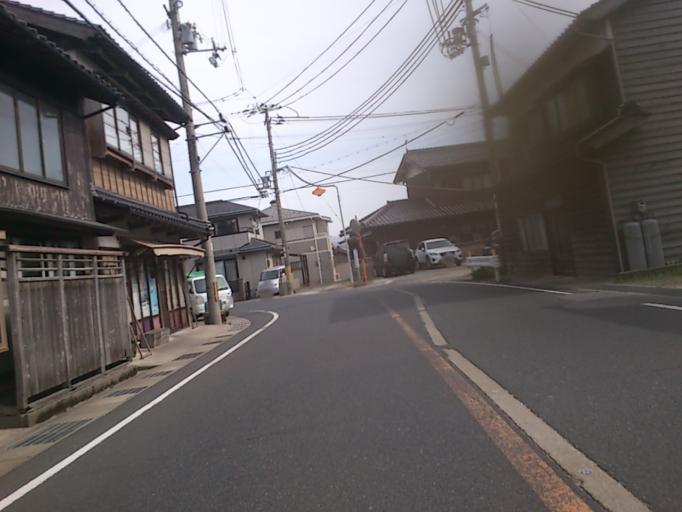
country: JP
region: Kyoto
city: Miyazu
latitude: 35.6893
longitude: 135.0179
